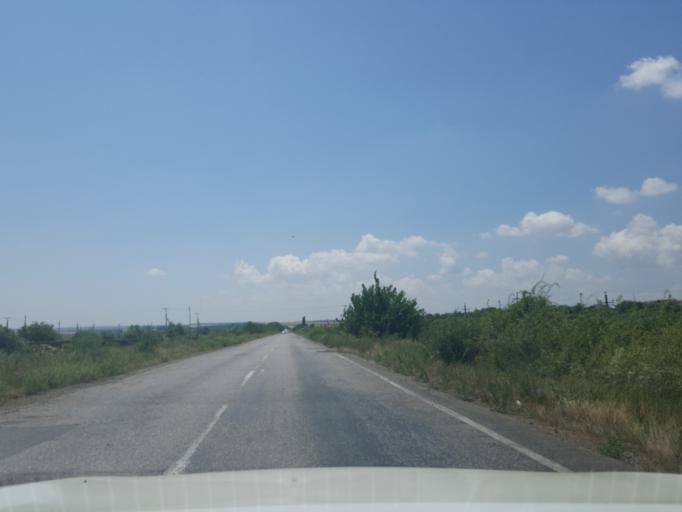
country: UA
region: Odessa
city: Bilyayivka
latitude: 46.4054
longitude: 30.1043
